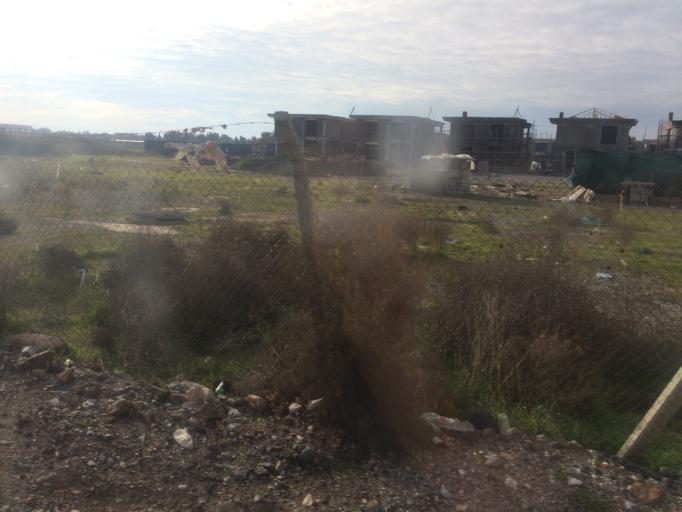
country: TR
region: Izmir
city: Menemen
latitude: 38.4979
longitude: 26.9600
